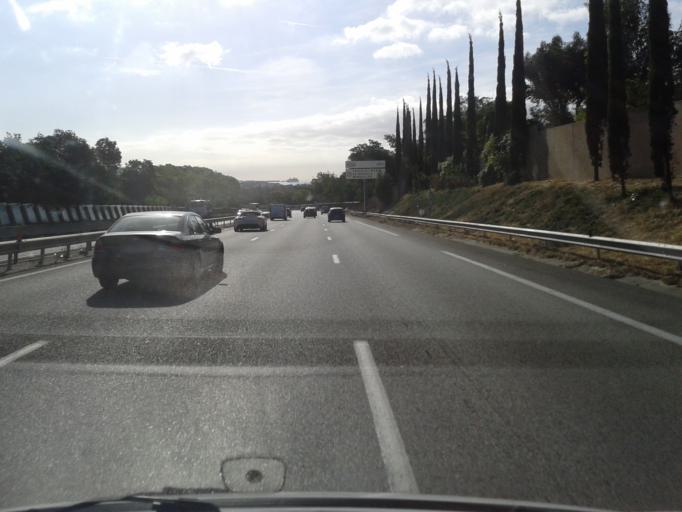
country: FR
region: Provence-Alpes-Cote d'Azur
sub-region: Departement des Alpes-Maritimes
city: Mandelieu-la-Napoule
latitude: 43.5411
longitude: 6.9289
